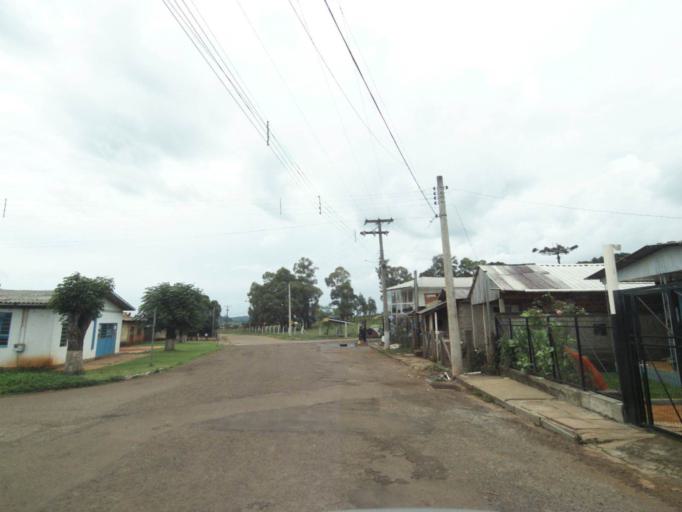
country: BR
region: Rio Grande do Sul
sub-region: Lagoa Vermelha
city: Lagoa Vermelha
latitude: -28.2262
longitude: -51.5149
